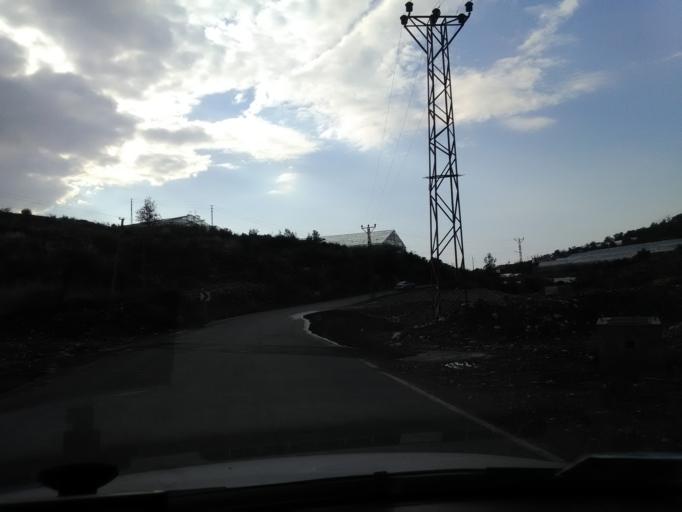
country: TR
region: Antalya
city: Gazipasa
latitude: 36.2777
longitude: 32.3575
